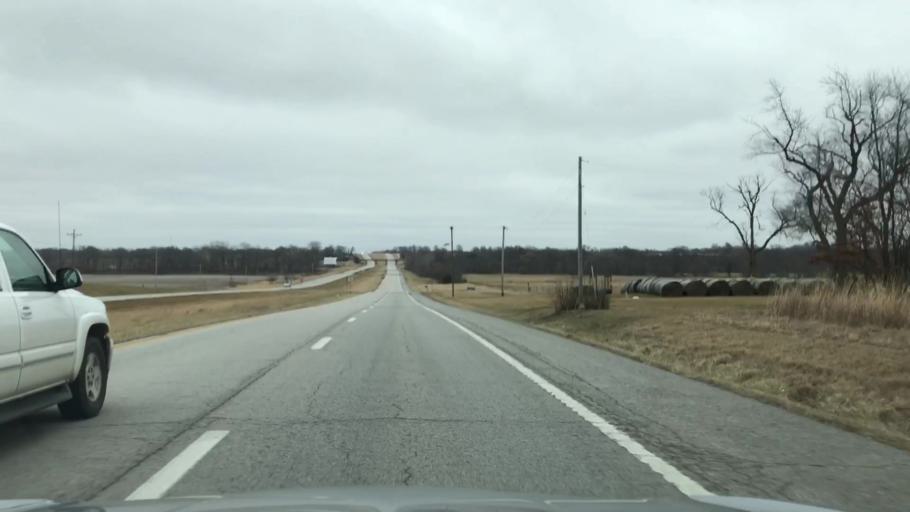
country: US
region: Missouri
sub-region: Linn County
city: Brookfield
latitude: 39.7785
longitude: -93.1564
